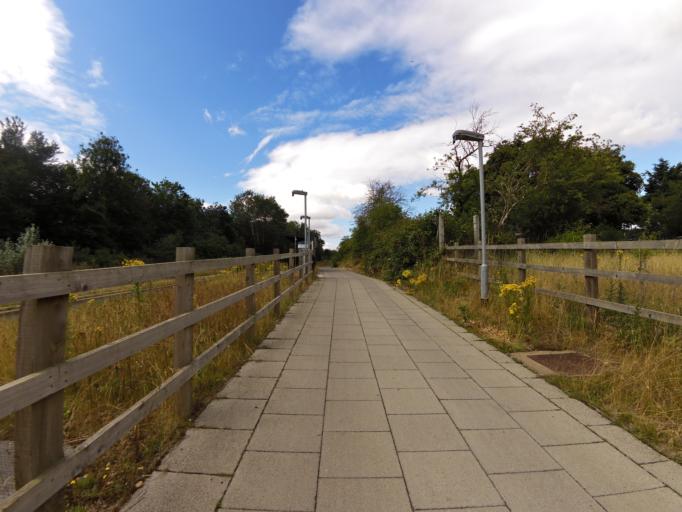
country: GB
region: England
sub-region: Cambridgeshire
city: Cambridge
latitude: 52.1720
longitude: 0.1217
